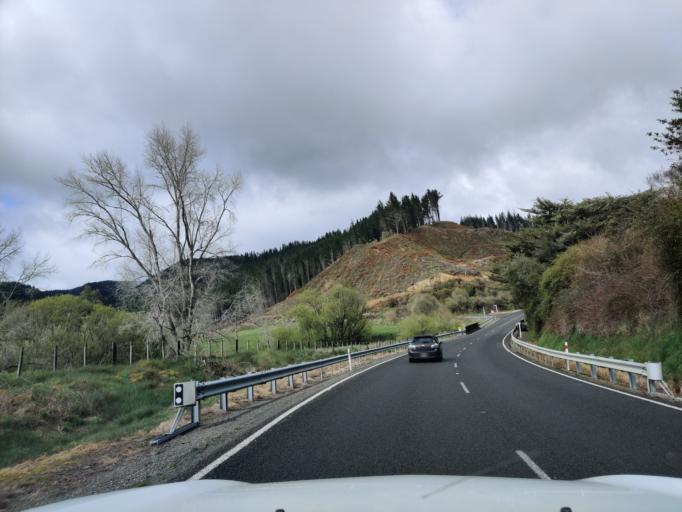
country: NZ
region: Waikato
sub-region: Otorohanga District
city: Otorohanga
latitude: -38.6144
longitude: 175.2194
